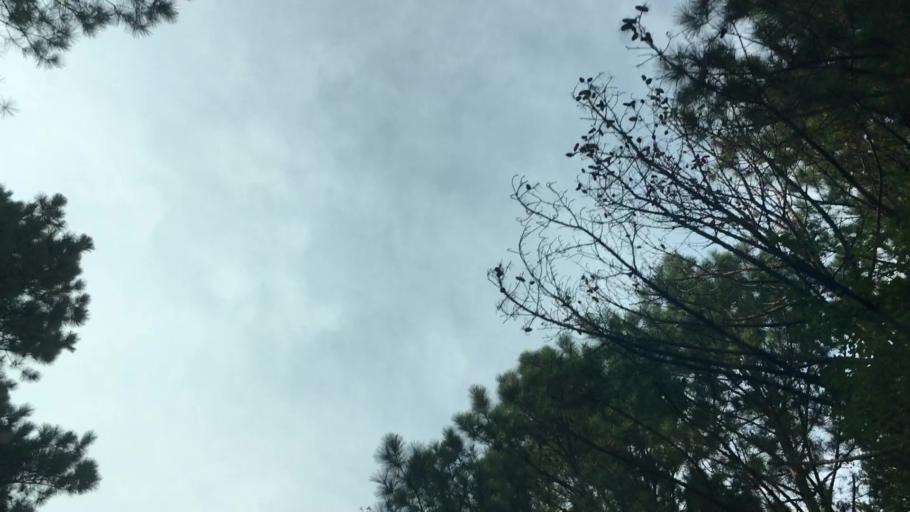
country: US
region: Alabama
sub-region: Bibb County
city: Woodstock
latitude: 33.2353
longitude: -87.1450
